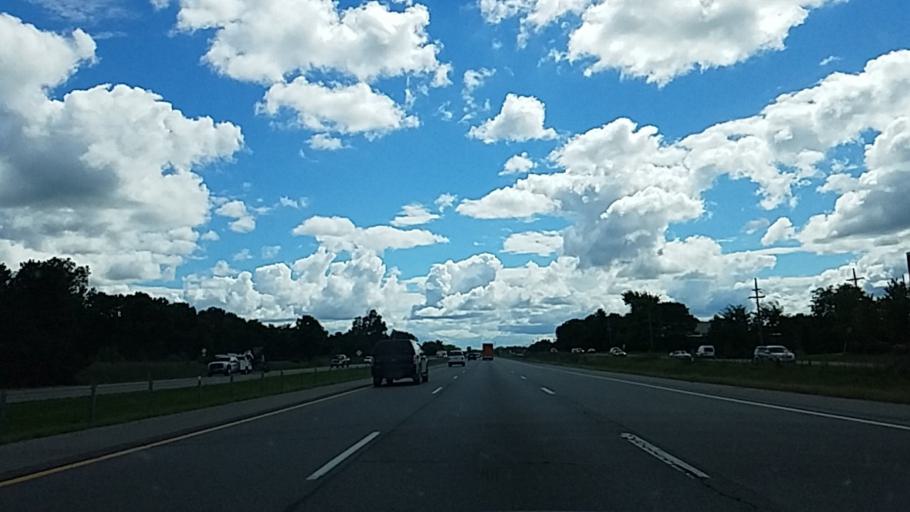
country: US
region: Michigan
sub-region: Livingston County
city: Brighton
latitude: 42.5025
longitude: -83.7581
